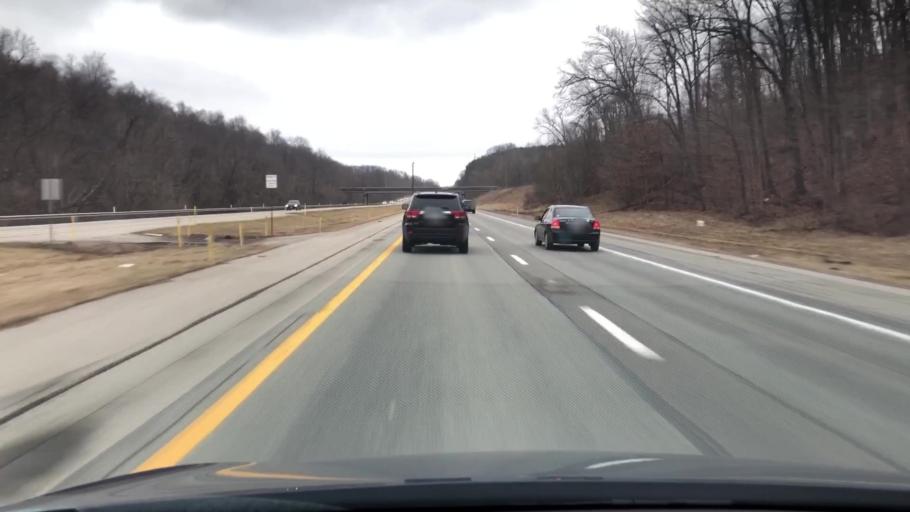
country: US
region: Pennsylvania
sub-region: Washington County
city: East Washington
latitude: 40.0510
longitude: -80.1840
